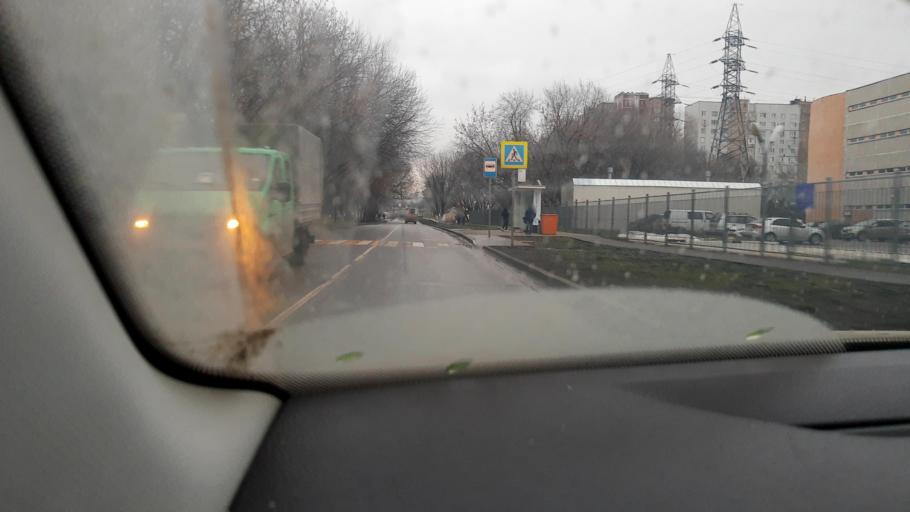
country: RU
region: Moskovskaya
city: Kur'yanovo
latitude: 55.6620
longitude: 37.7032
